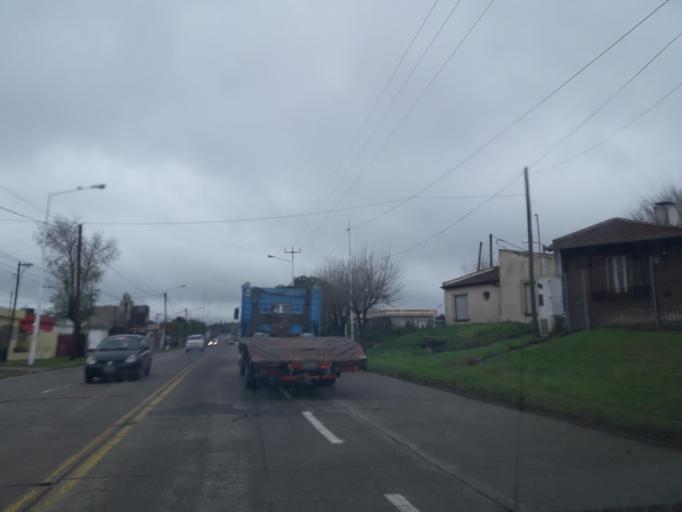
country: AR
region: Buenos Aires
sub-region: Partido de Tandil
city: Tandil
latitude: -37.3173
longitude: -59.1551
